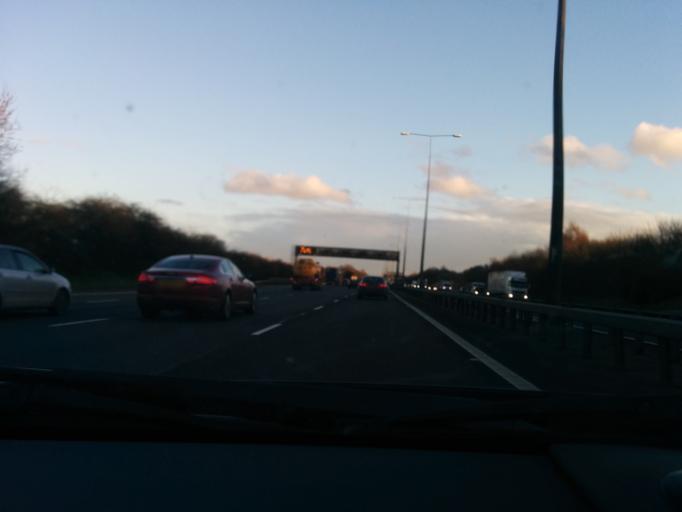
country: GB
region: England
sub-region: Buckinghamshire
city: Seer Green
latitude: 51.5904
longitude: -0.6143
